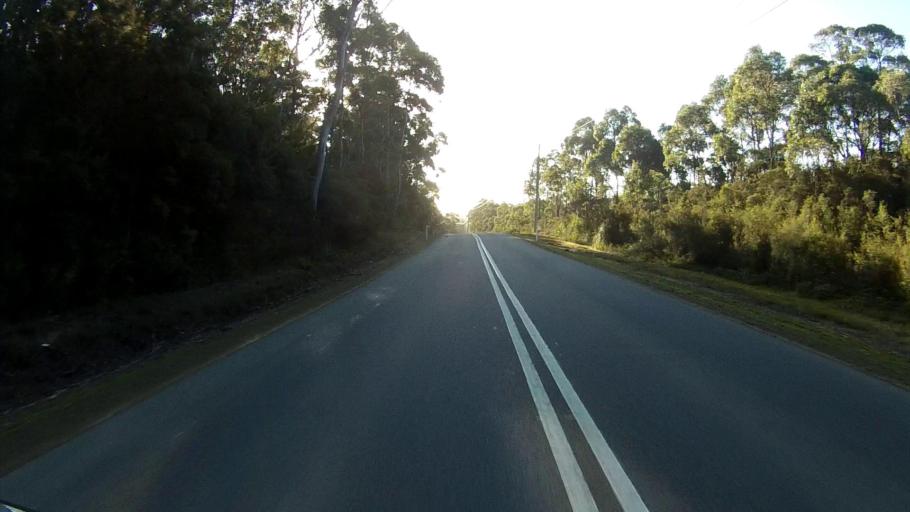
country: AU
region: Tasmania
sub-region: Clarence
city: Sandford
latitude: -43.0851
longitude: 147.8669
